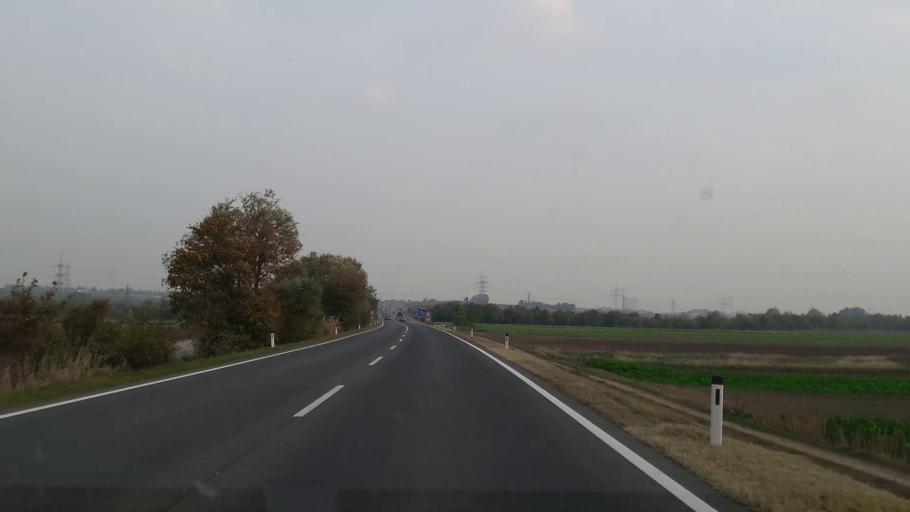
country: AT
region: Burgenland
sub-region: Politischer Bezirk Neusiedl am See
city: Parndorf
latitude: 48.0074
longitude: 16.8270
